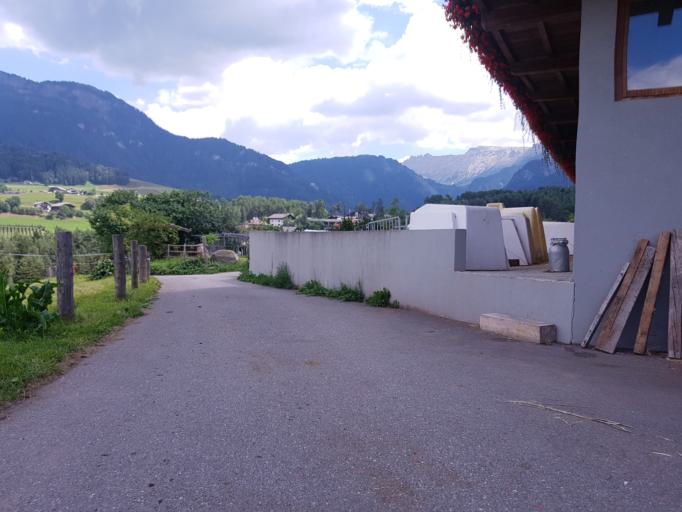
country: IT
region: Trentino-Alto Adige
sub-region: Bolzano
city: Castelrotto
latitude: 46.5584
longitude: 11.5494
